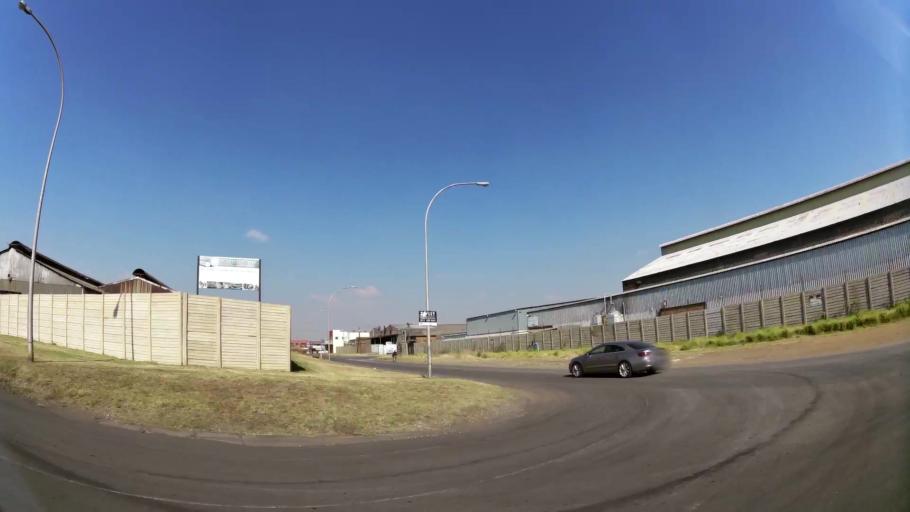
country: ZA
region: Gauteng
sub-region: Ekurhuleni Metropolitan Municipality
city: Benoni
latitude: -26.2082
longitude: 28.3008
